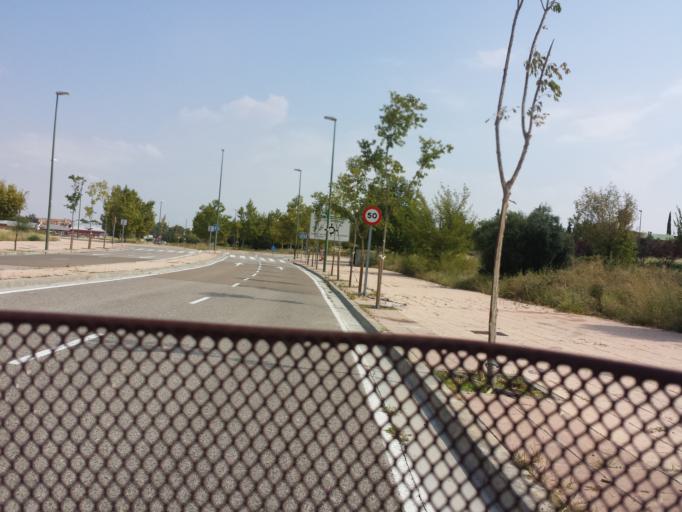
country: ES
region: Aragon
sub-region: Provincia de Zaragoza
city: Montecanal
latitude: 41.6325
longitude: -0.9427
